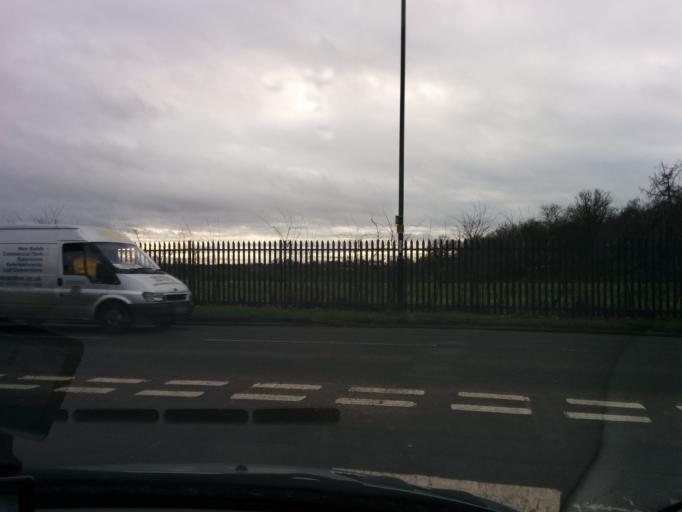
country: GB
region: England
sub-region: Warwickshire
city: Kenilworth
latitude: 52.3933
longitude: -1.5793
